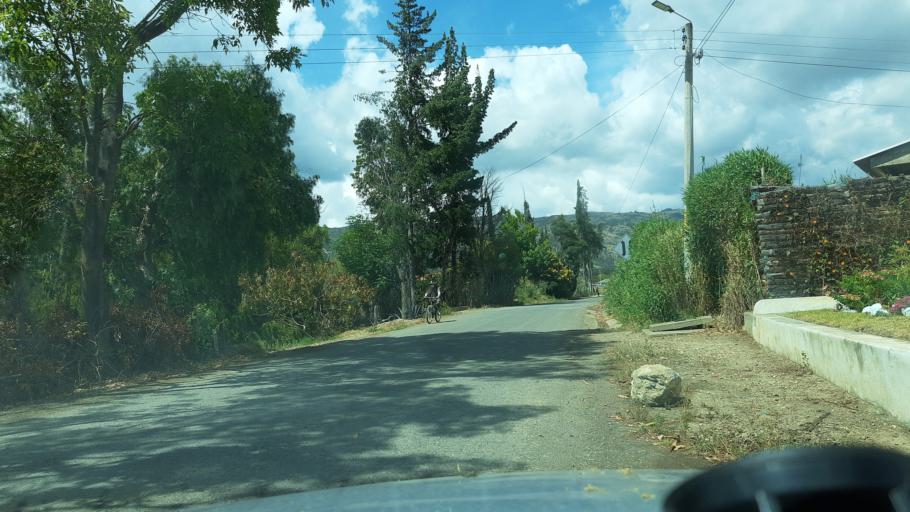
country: CO
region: Boyaca
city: Cucaita
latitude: 5.5509
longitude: -73.4553
